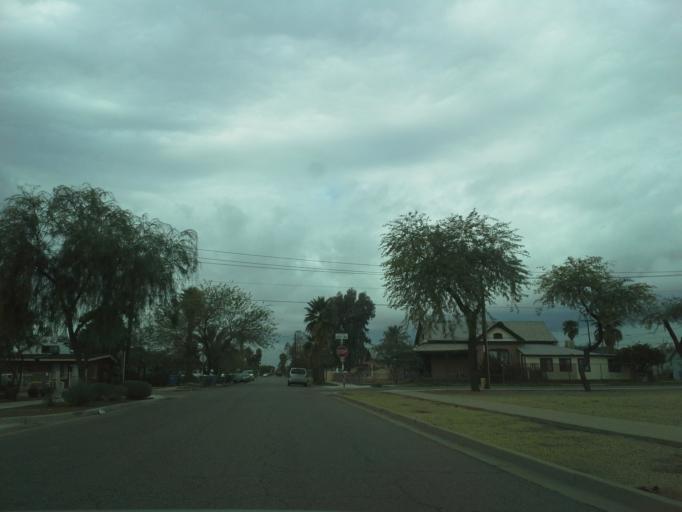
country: US
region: Arizona
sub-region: Maricopa County
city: Phoenix
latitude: 33.4460
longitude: -112.1017
